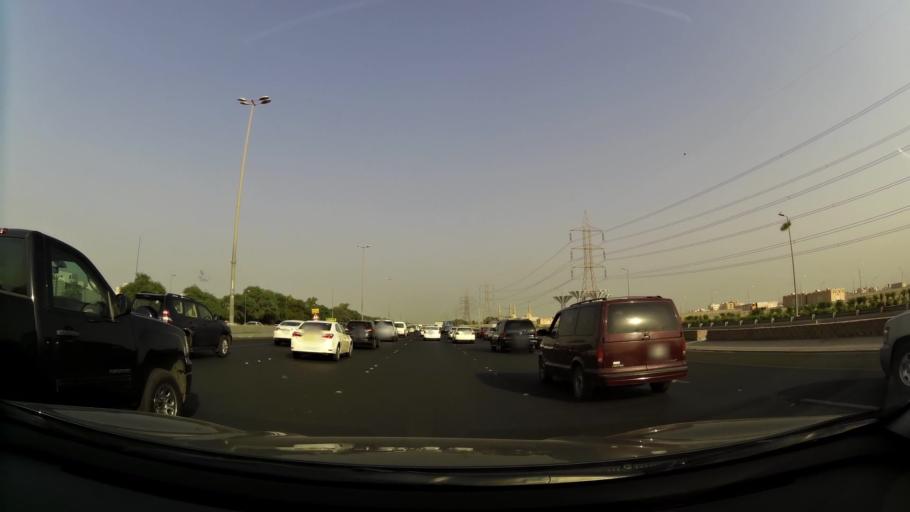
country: KW
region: Al Farwaniyah
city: Janub as Surrah
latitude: 29.3045
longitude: 47.9889
